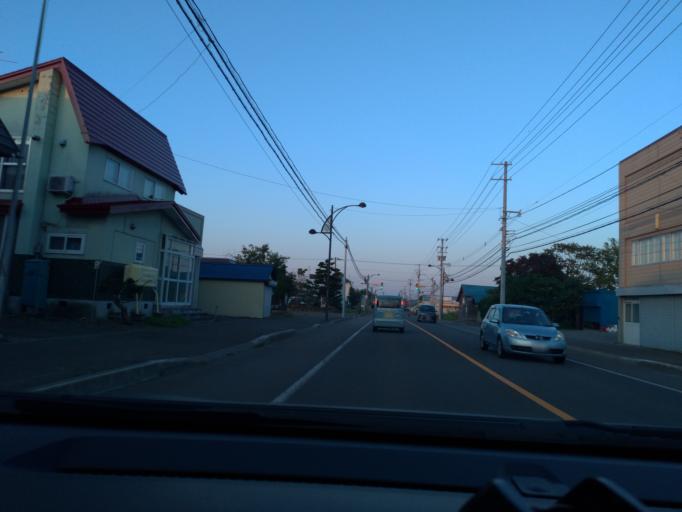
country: JP
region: Hokkaido
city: Iwamizawa
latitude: 43.3314
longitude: 141.6646
